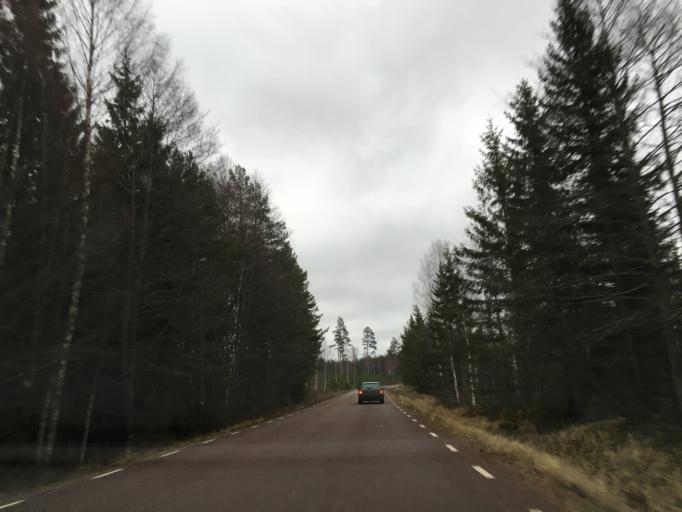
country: SE
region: Uppsala
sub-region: Alvkarleby Kommun
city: Skutskaer
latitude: 60.6218
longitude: 17.4547
